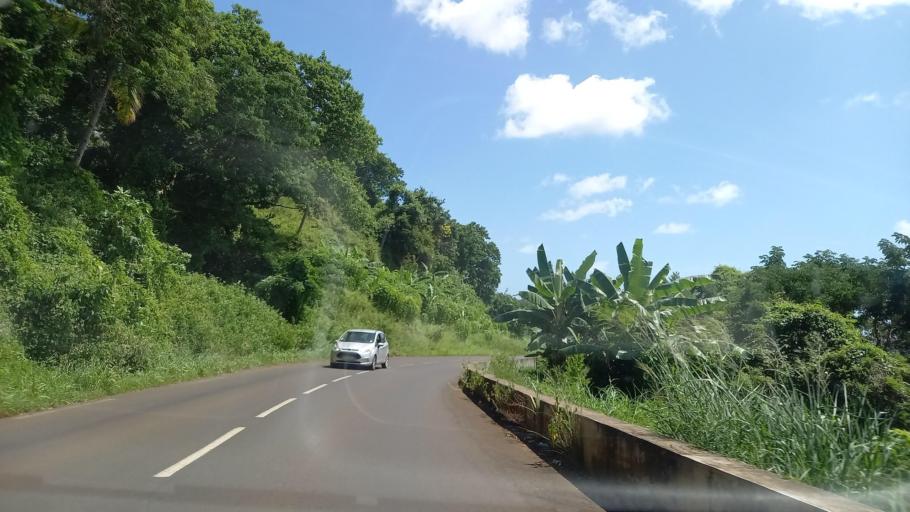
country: YT
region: Bandraboua
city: Bandraboua
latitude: -12.7138
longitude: 45.1270
